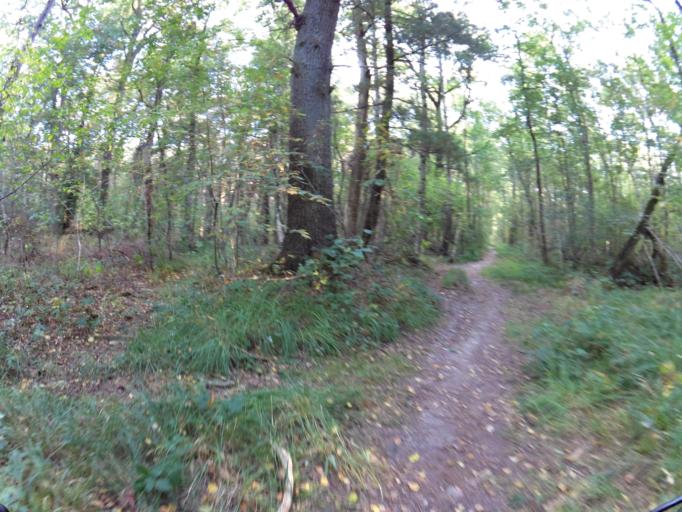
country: DE
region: North Rhine-Westphalia
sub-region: Regierungsbezirk Koln
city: Gangelt
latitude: 50.9708
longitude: 6.0128
